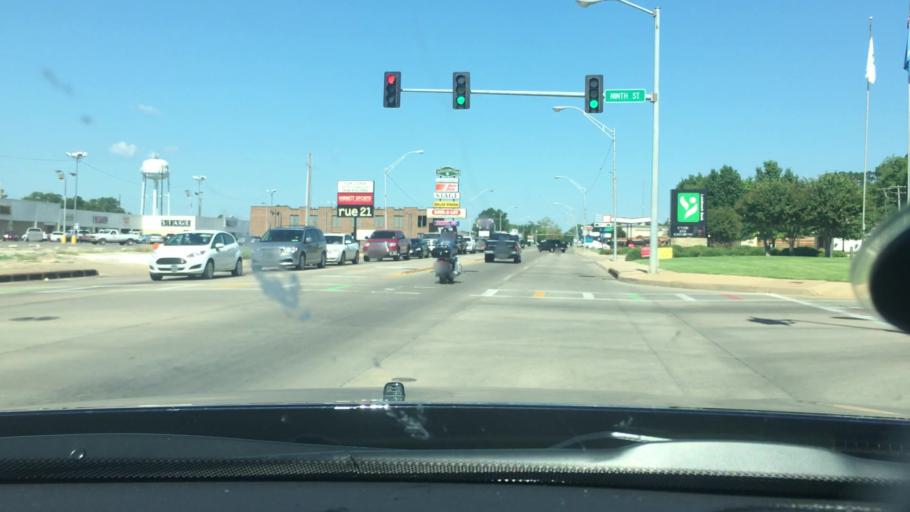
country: US
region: Oklahoma
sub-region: Bryan County
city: Durant
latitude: 33.9931
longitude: -96.3853
